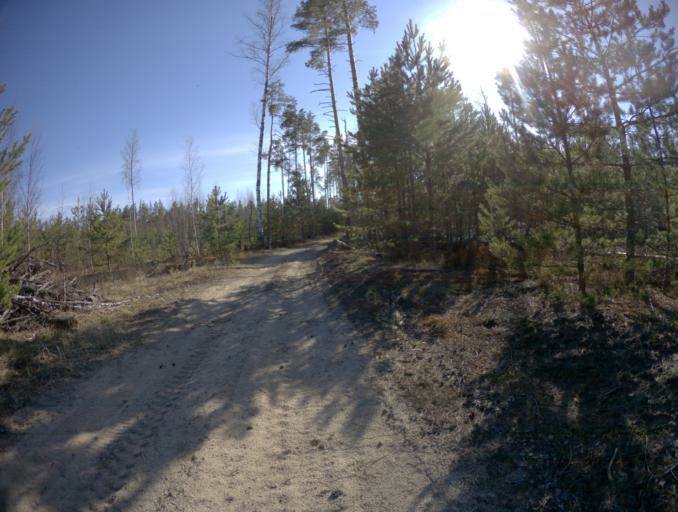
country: RU
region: Vladimir
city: Ivanishchi
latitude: 55.6995
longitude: 40.4342
